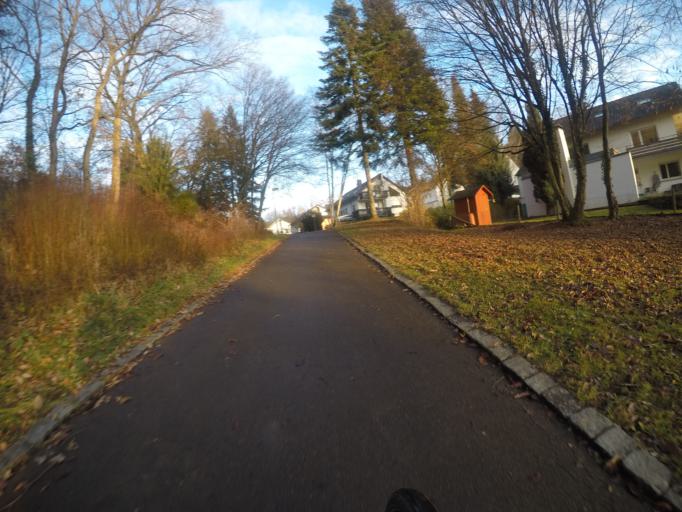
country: DE
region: Baden-Wuerttemberg
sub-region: Tuebingen Region
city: Tuebingen
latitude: 48.5333
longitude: 9.0858
